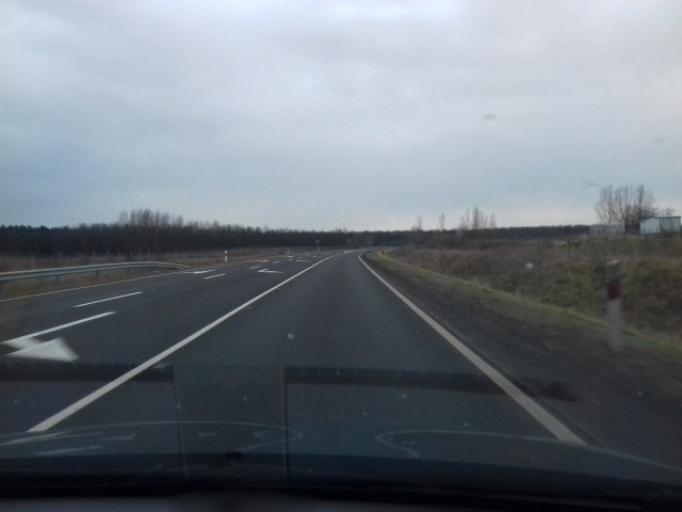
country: HU
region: Szabolcs-Szatmar-Bereg
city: Nyirpazony
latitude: 48.0115
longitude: 21.8441
